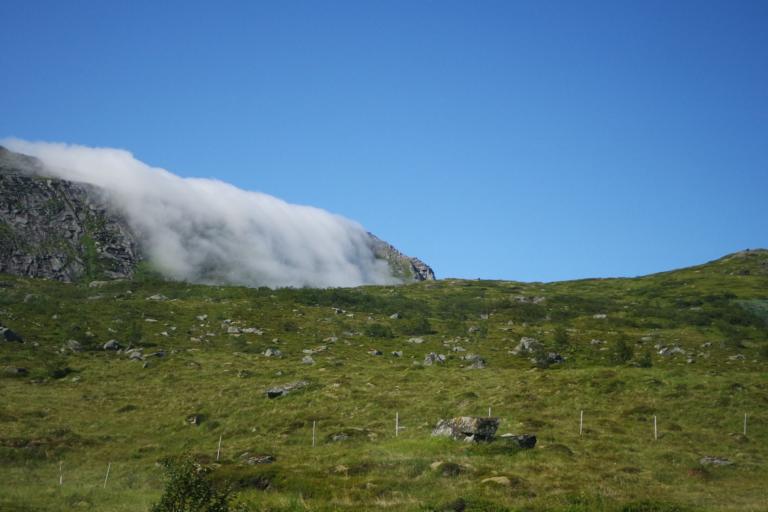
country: NO
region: Nordland
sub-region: Flakstad
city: Ramberg
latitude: 68.0841
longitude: 13.2931
